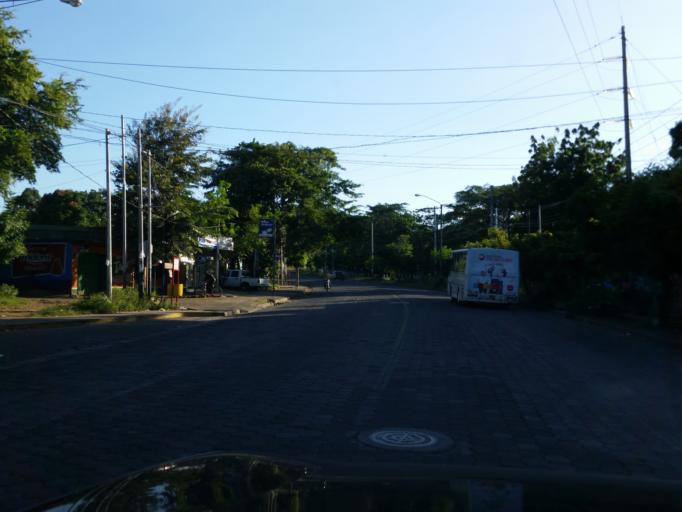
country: NI
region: Managua
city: Ciudad Sandino
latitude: 12.1402
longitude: -86.3075
